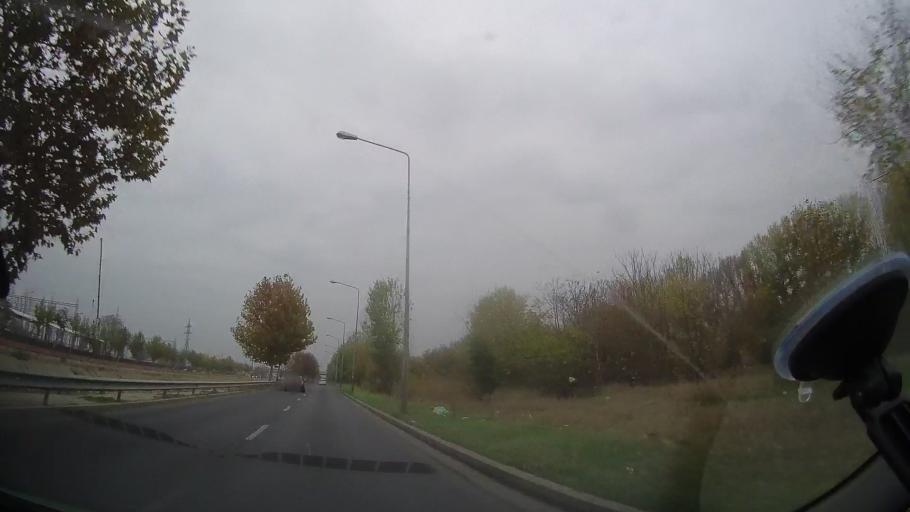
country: RO
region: Ilfov
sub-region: Comuna Popesti-Leordeni
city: Popesti-Leordeni
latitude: 44.4003
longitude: 26.1540
